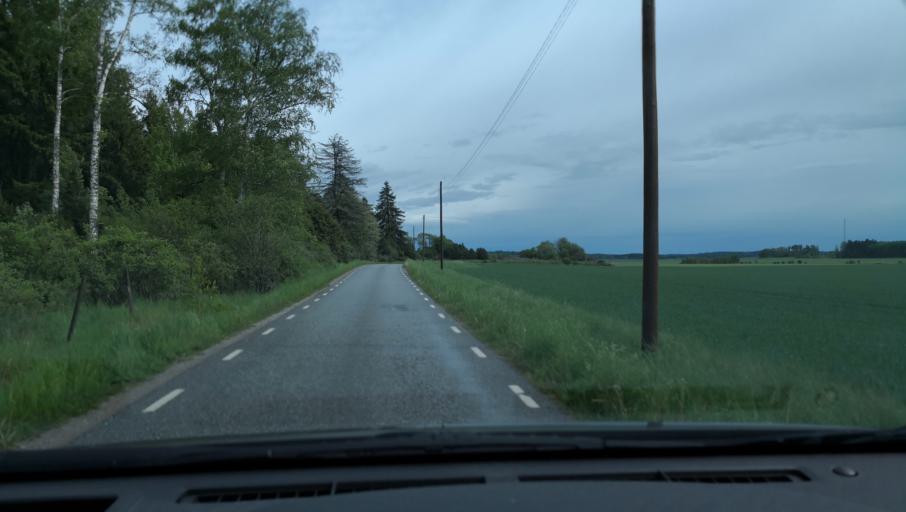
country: SE
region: Uppsala
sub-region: Enkopings Kommun
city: Orsundsbro
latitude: 59.7066
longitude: 17.3950
